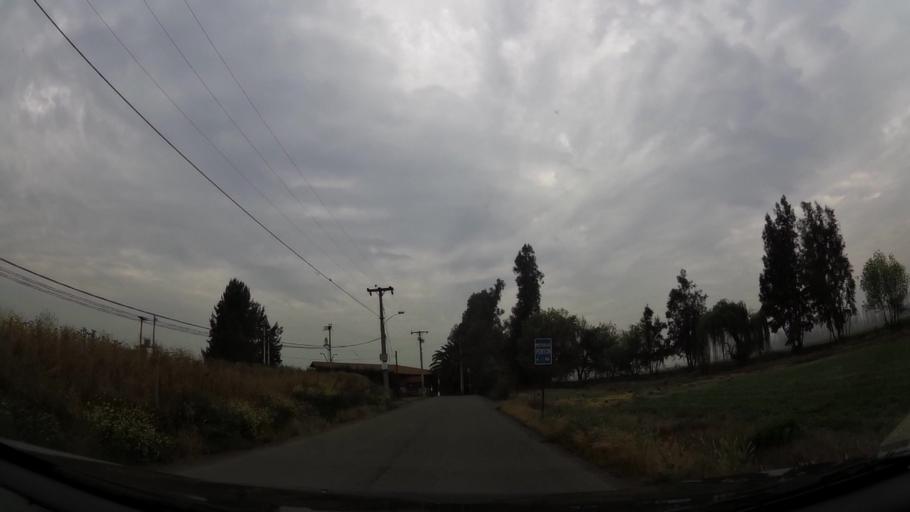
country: CL
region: Santiago Metropolitan
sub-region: Provincia de Chacabuco
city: Lampa
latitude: -33.2631
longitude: -70.7686
